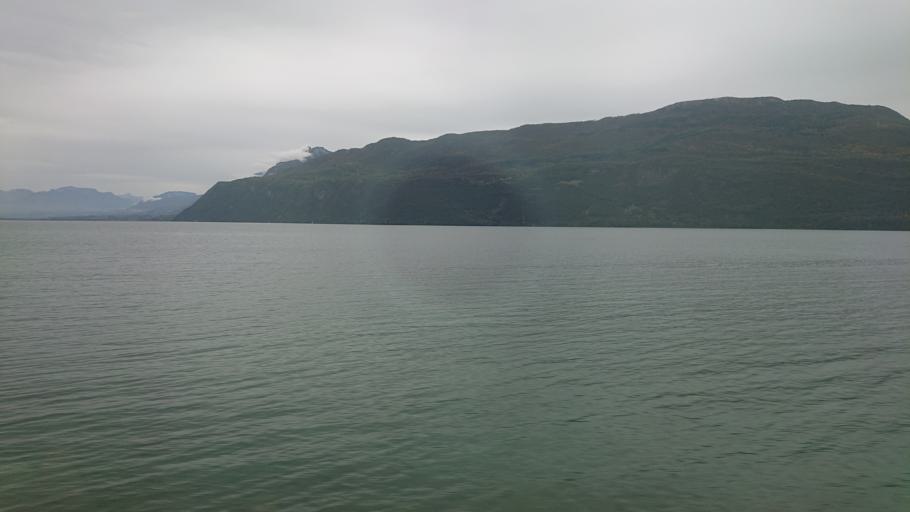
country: FR
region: Rhone-Alpes
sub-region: Departement de la Savoie
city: Brison-Saint-Innocent
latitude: 45.7554
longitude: 5.8771
